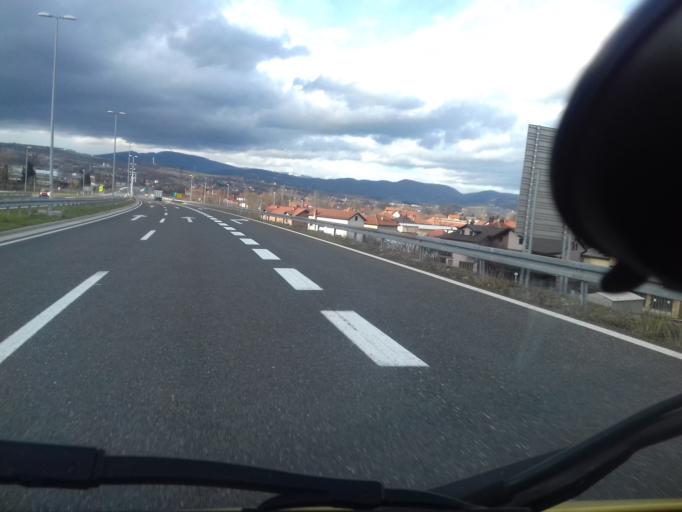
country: BA
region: Federation of Bosnia and Herzegovina
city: Visoko
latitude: 44.0050
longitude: 18.1716
